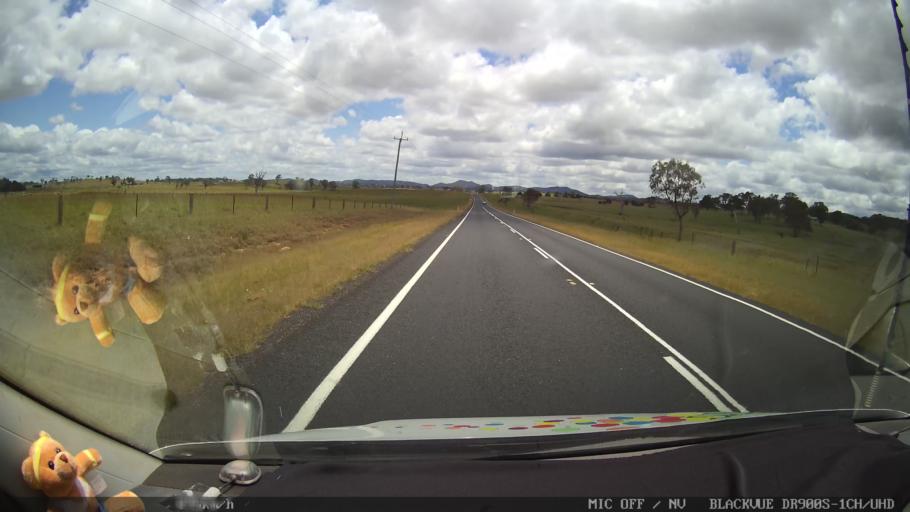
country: AU
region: New South Wales
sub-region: Glen Innes Severn
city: Glen Innes
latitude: -29.4211
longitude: 151.8611
